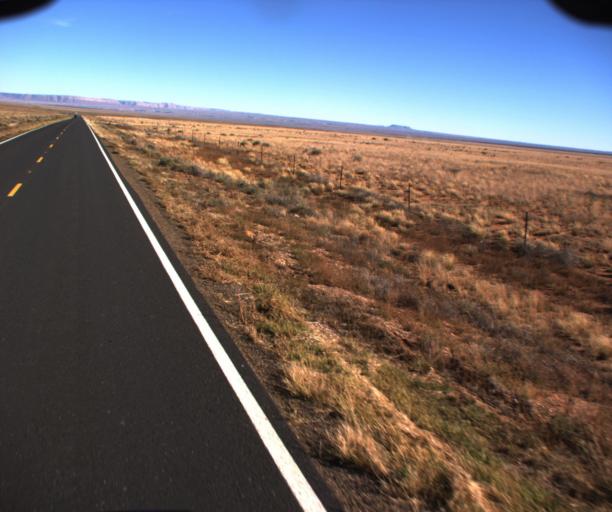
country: US
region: Arizona
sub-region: Coconino County
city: Fredonia
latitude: 36.7218
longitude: -112.0154
